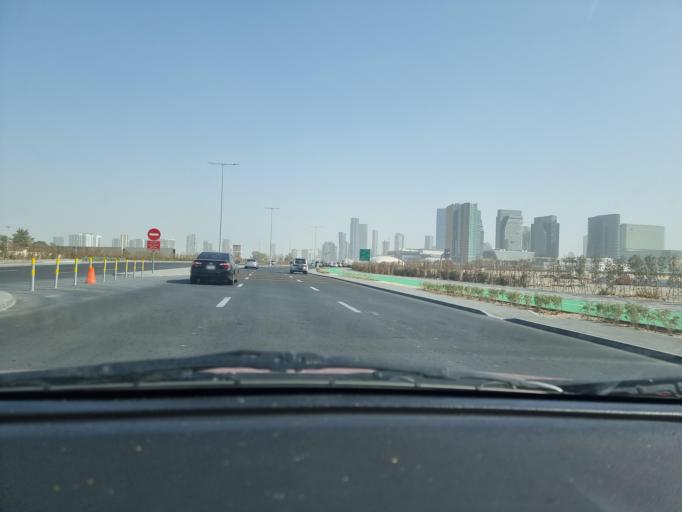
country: AE
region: Abu Dhabi
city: Abu Dhabi
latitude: 24.5088
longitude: 54.3794
